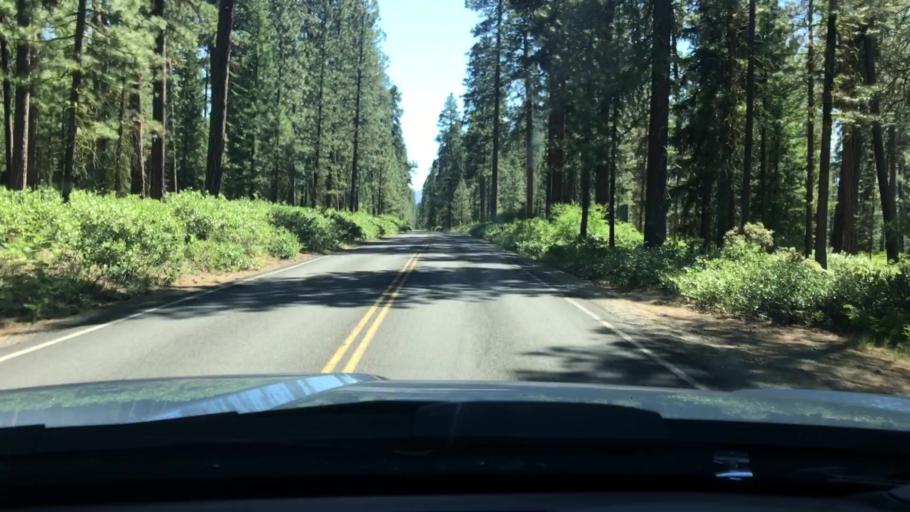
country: US
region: Oregon
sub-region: Deschutes County
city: Sisters
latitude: 44.4196
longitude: -121.6690
